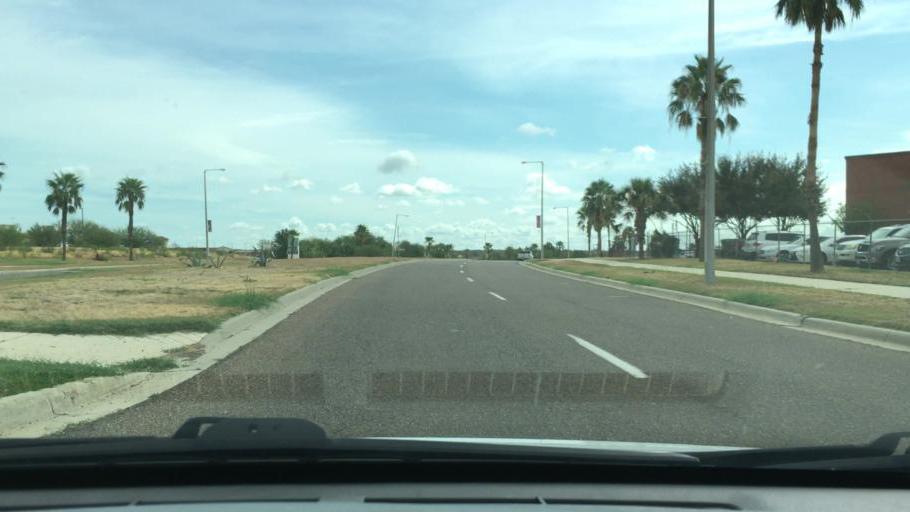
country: US
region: Texas
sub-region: Webb County
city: Laredo
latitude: 27.6040
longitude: -99.4804
